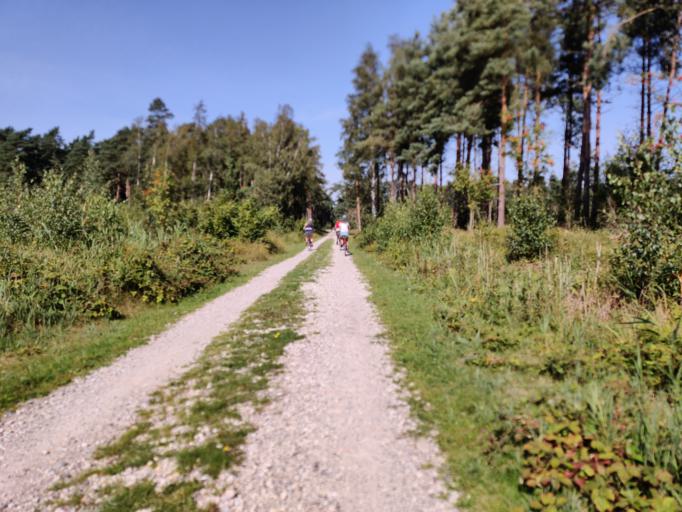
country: DK
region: Zealand
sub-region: Guldborgsund Kommune
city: Nykobing Falster
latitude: 54.6288
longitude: 11.9585
